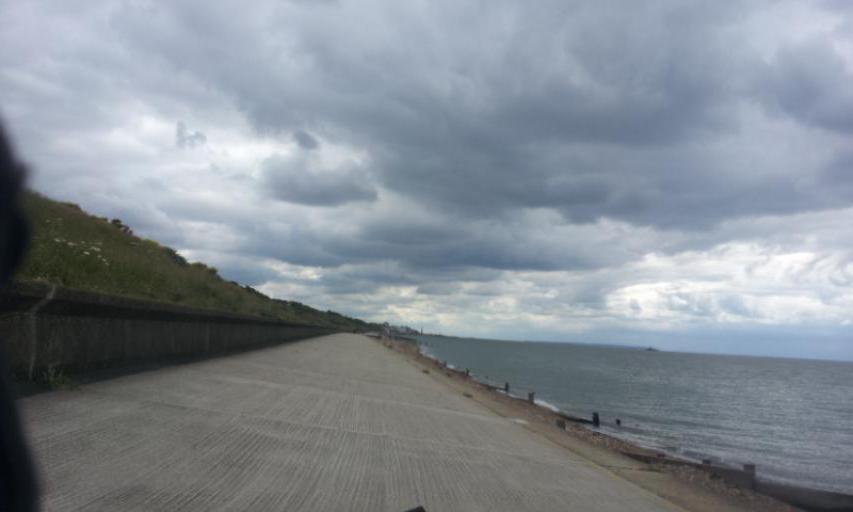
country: GB
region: England
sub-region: Kent
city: Herne Bay
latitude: 51.3742
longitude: 1.1637
